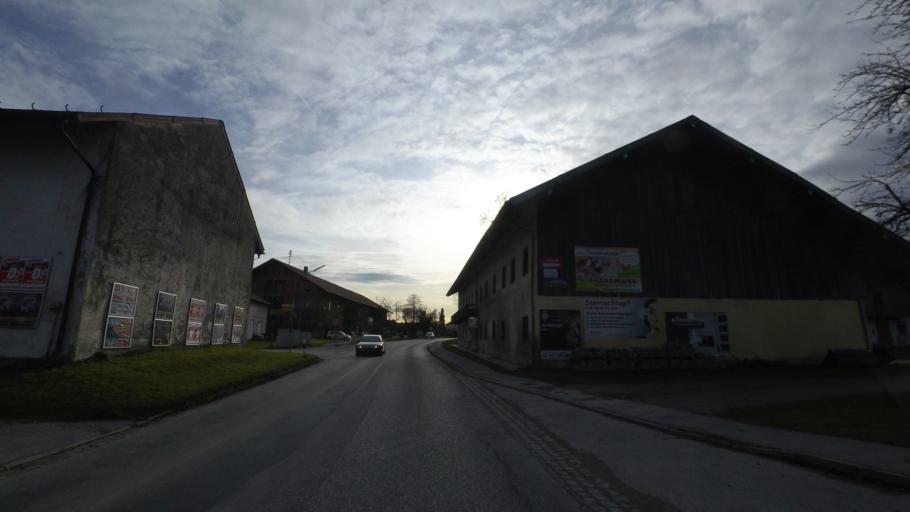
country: DE
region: Bavaria
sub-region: Upper Bavaria
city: Prutting
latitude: 47.8872
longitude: 12.1899
